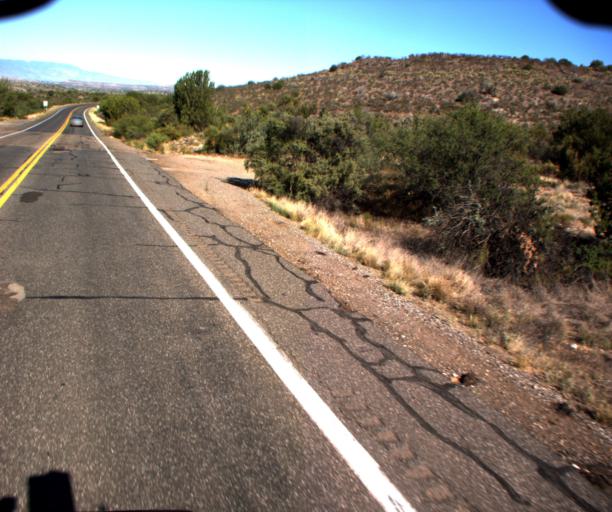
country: US
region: Arizona
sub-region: Yavapai County
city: Lake Montezuma
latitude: 34.6909
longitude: -111.7462
